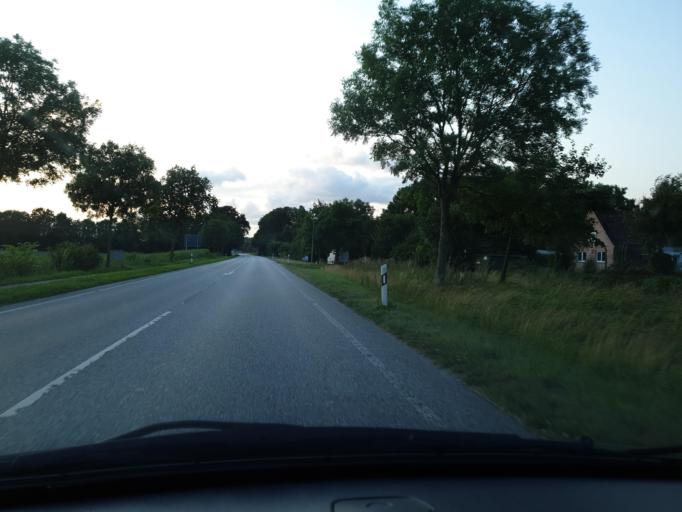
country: DE
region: Schleswig-Holstein
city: Schmedeswurth
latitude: 53.9195
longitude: 9.0474
